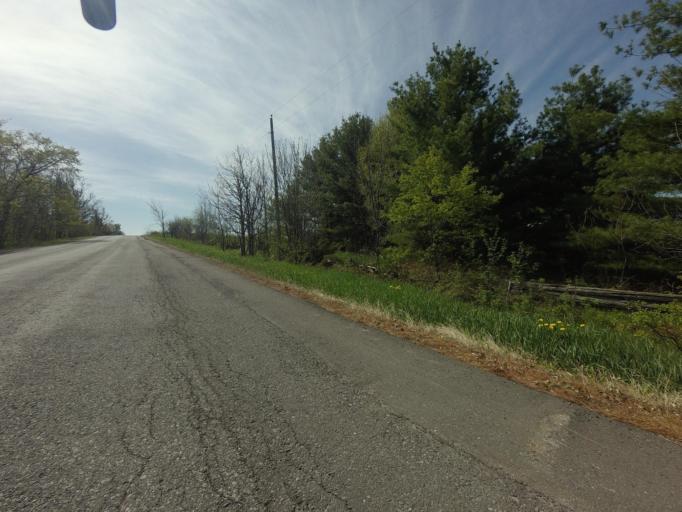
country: CA
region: Ontario
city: Arnprior
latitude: 45.4248
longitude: -76.2317
